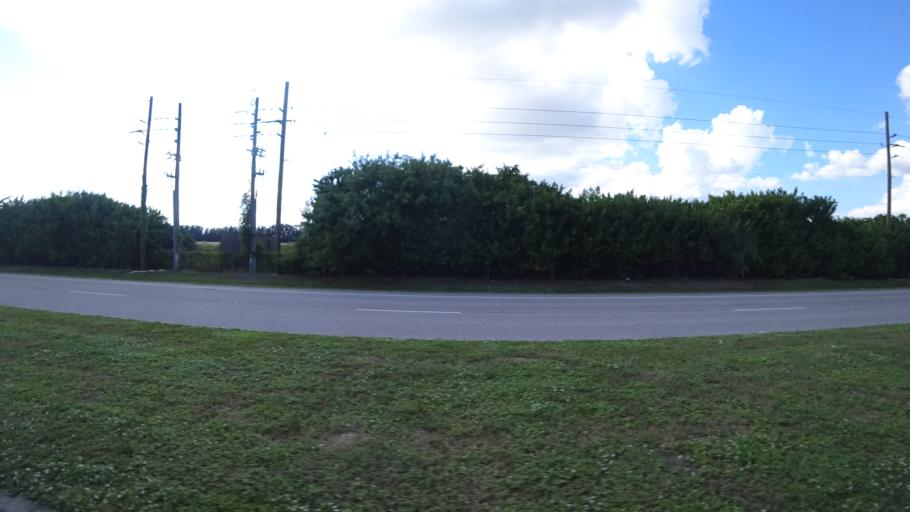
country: US
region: Florida
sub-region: Manatee County
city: Longboat Key
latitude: 27.4573
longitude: -82.6369
